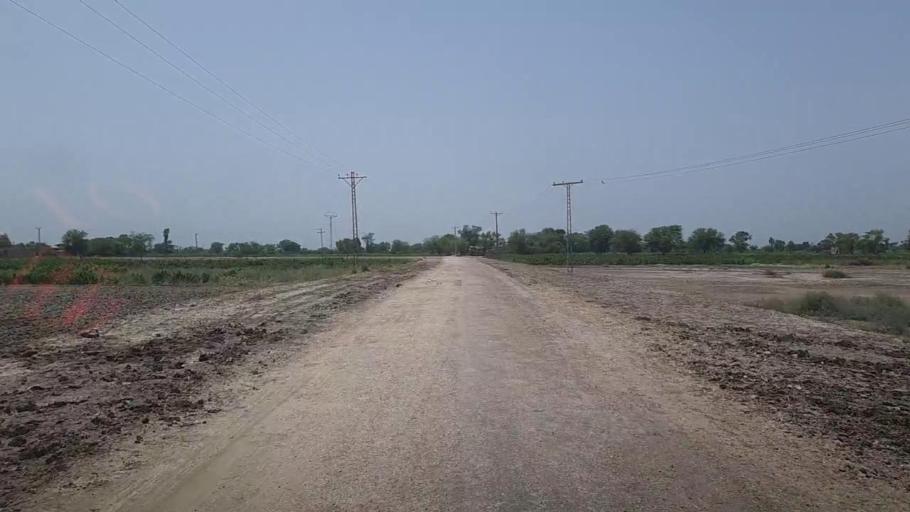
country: PK
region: Sindh
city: Pad Idan
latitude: 26.8343
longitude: 68.3107
